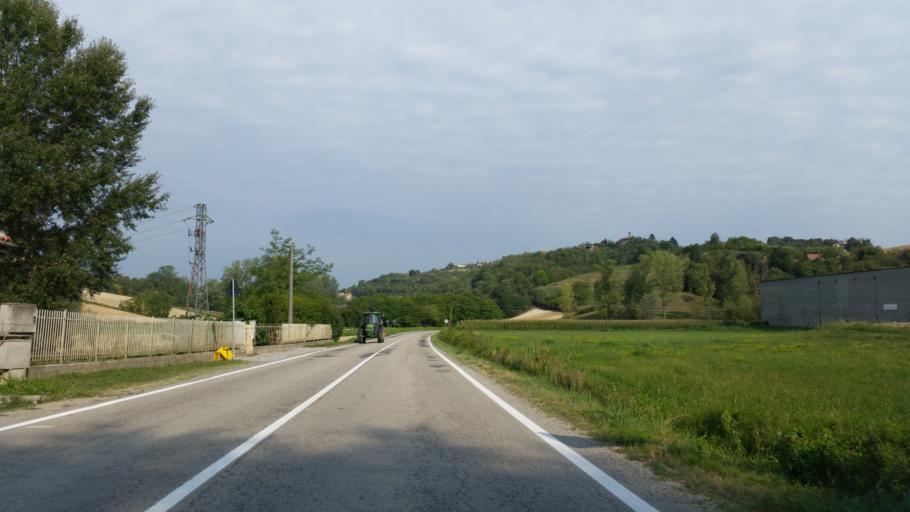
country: IT
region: Piedmont
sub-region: Provincia di Asti
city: Montiglio
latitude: 45.0710
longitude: 8.1059
